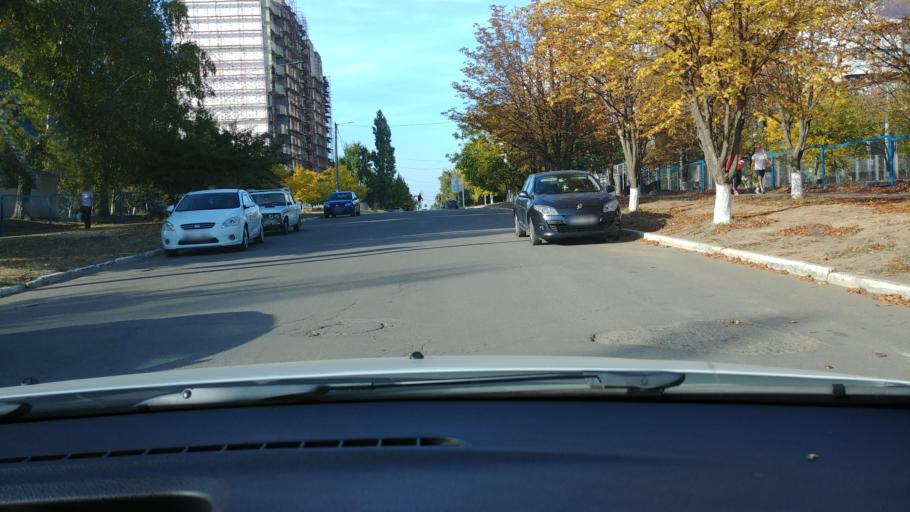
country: MD
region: Rezina
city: Rezina
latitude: 47.7470
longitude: 28.9561
